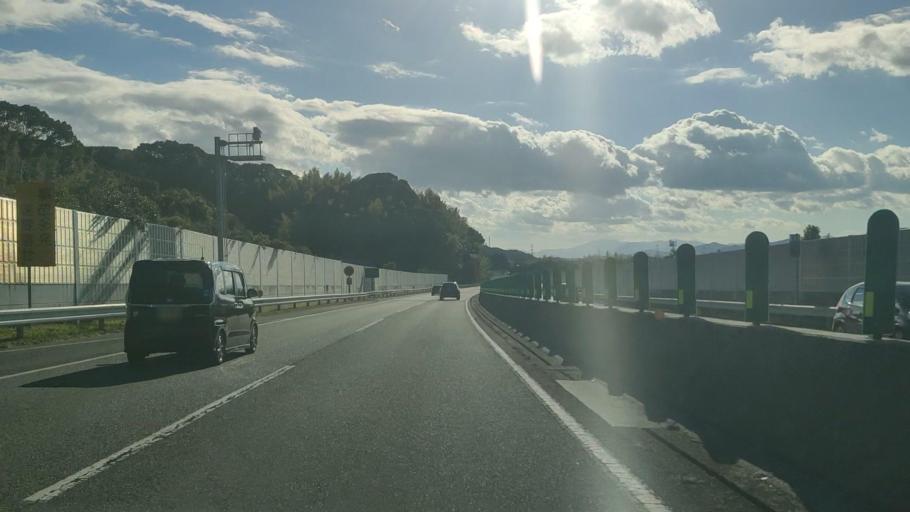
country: JP
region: Fukuoka
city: Nakama
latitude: 33.8288
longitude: 130.7651
